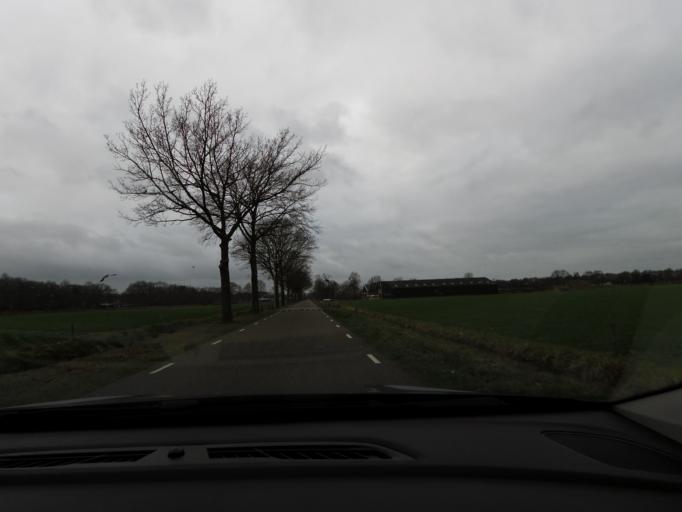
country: NL
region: North Brabant
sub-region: Gemeente Heusden
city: Heusden
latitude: 51.6727
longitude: 5.1494
